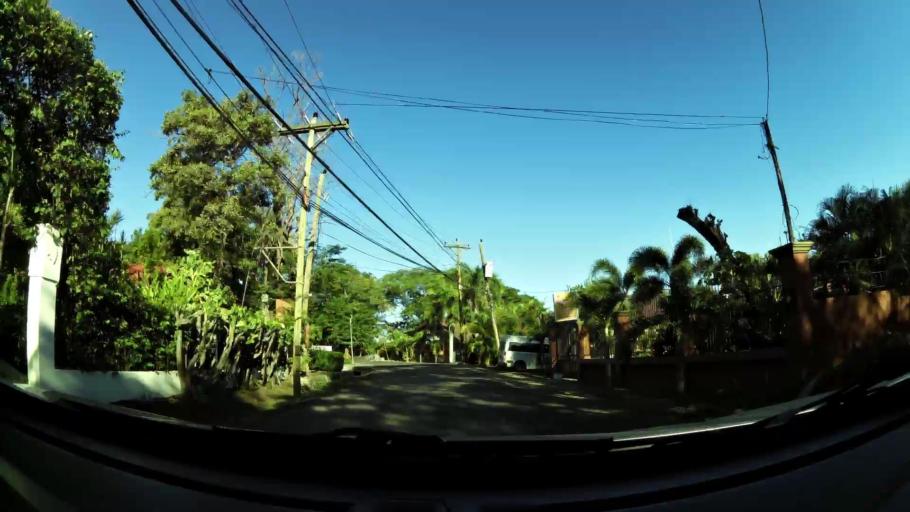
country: CR
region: Guanacaste
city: Sardinal
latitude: 10.5686
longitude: -85.6768
